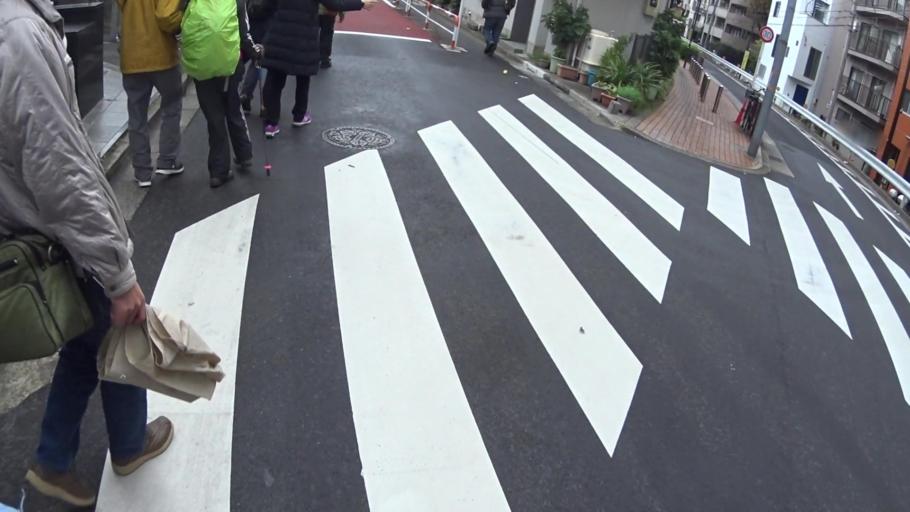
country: JP
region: Tokyo
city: Tokyo
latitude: 35.6983
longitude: 139.7116
